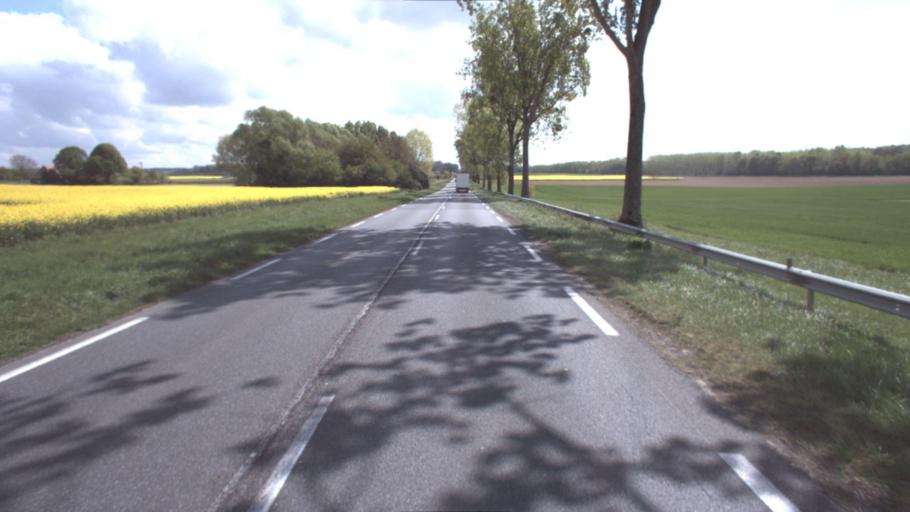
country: FR
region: Ile-de-France
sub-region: Departement de Seine-et-Marne
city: La Ferte-Gaucher
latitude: 48.6957
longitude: 3.3030
